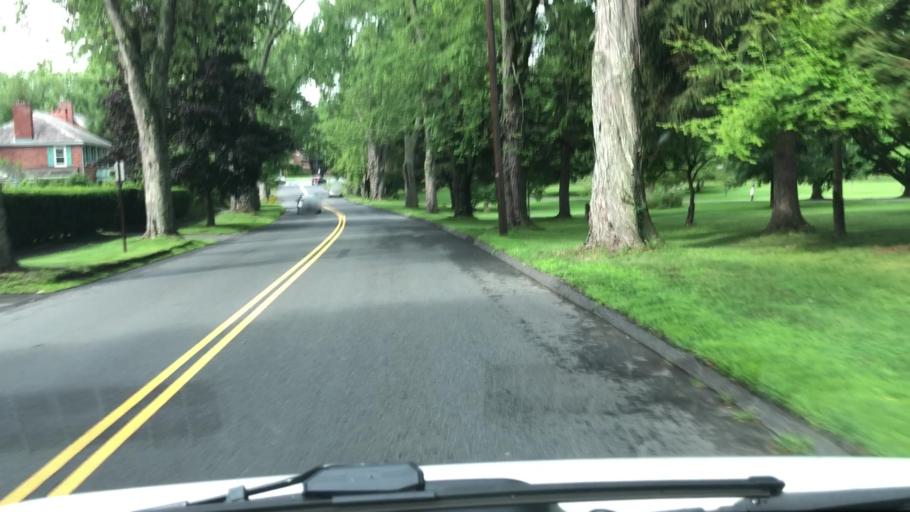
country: US
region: Massachusetts
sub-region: Hampshire County
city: Northampton
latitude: 42.3265
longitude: -72.6477
